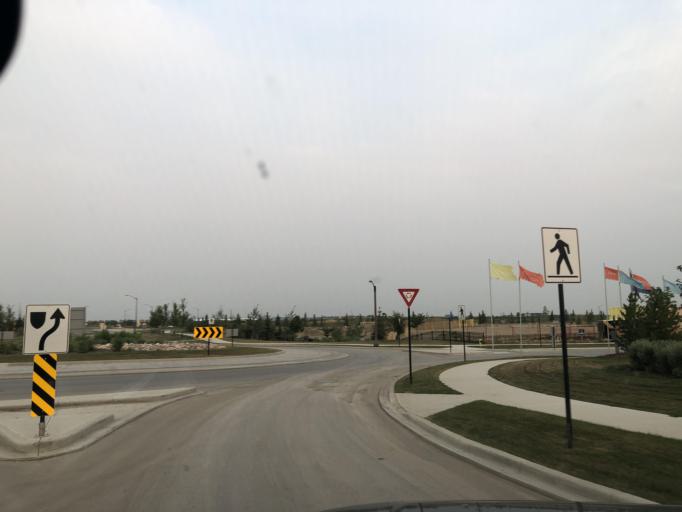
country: CA
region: Alberta
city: Cochrane
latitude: 51.1213
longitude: -114.3908
